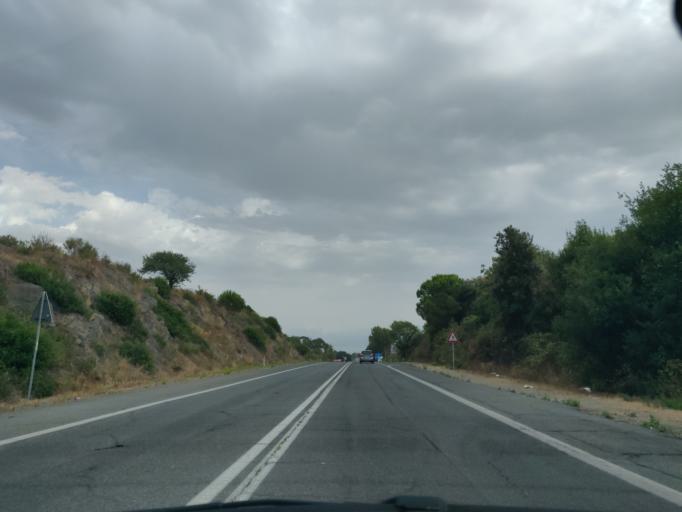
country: IT
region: Latium
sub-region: Citta metropolitana di Roma Capitale
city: Santa Marinella
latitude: 42.0308
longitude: 11.9372
